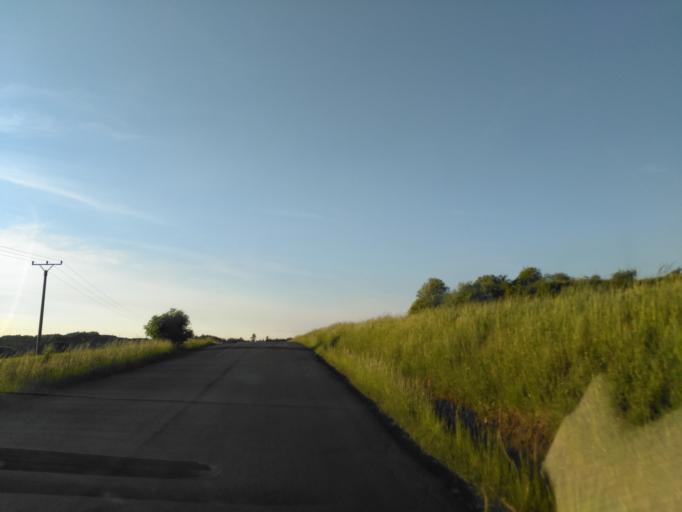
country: CZ
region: Central Bohemia
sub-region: Okres Beroun
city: Beroun
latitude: 49.9224
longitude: 14.0722
